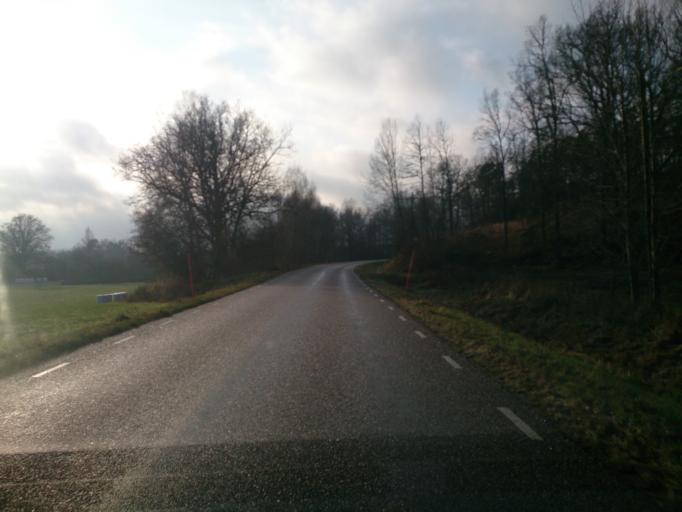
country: SE
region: OEstergoetland
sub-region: Atvidabergs Kommun
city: Atvidaberg
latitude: 58.2273
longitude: 15.9938
